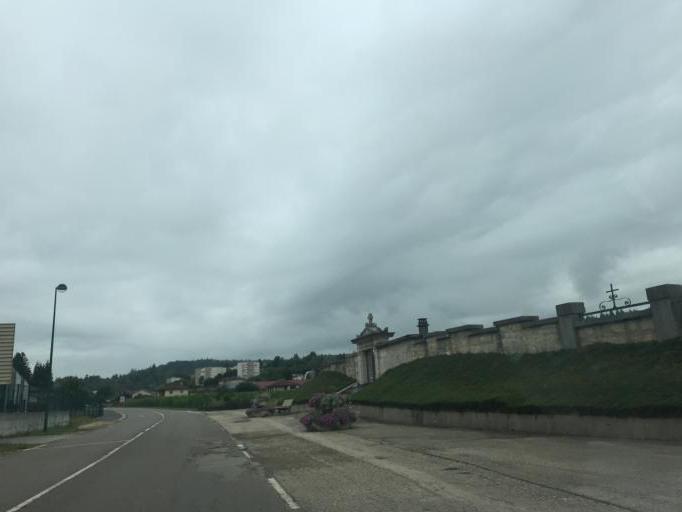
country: FR
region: Rhone-Alpes
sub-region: Departement de l'Ain
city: Arbent
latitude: 46.2857
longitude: 5.6753
